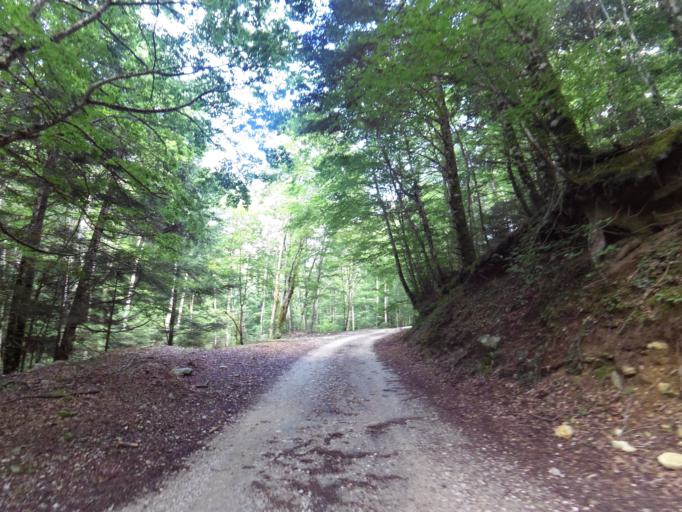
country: IT
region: Calabria
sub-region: Provincia di Vibo-Valentia
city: Nardodipace
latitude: 38.5224
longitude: 16.3814
